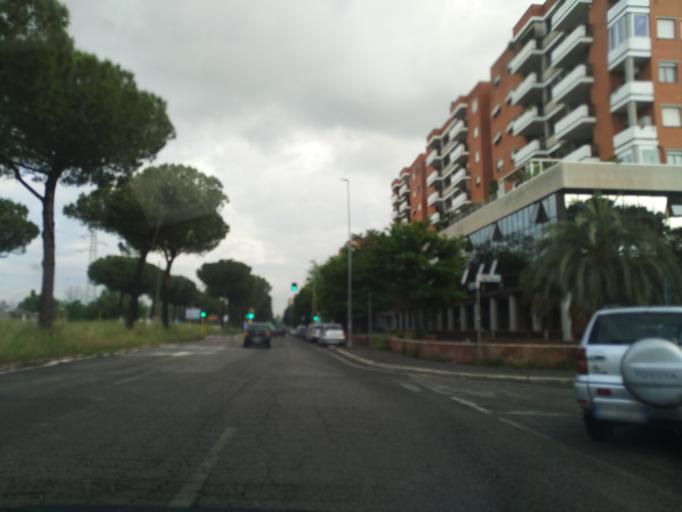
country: IT
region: Latium
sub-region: Citta metropolitana di Roma Capitale
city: Rome
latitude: 41.9188
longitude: 12.5673
